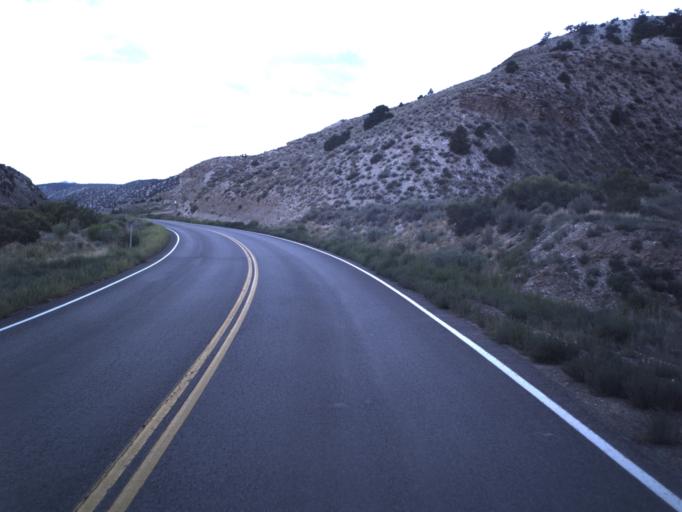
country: US
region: Utah
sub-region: Duchesne County
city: Duchesne
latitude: 40.1086
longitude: -110.4643
